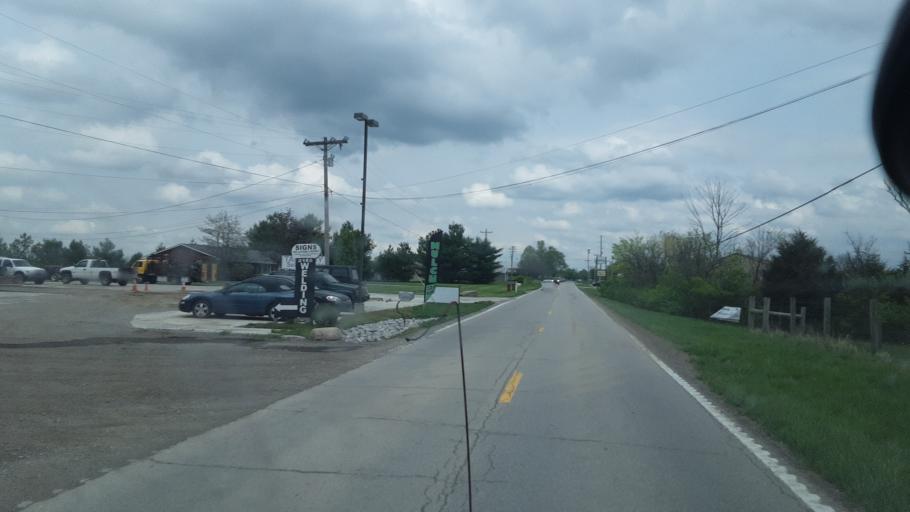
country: US
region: Kentucky
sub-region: Grant County
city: Dry Ridge
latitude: 38.6757
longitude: -84.6295
